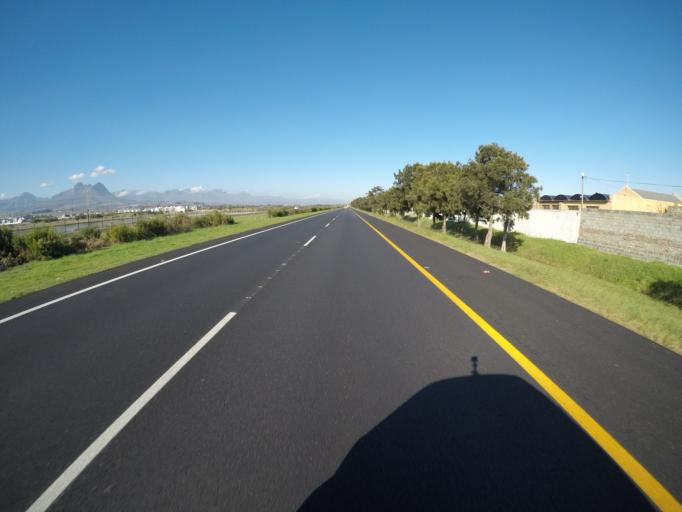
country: ZA
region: Western Cape
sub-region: Cape Winelands District Municipality
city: Stellenbosch
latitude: -34.0532
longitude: 18.7644
